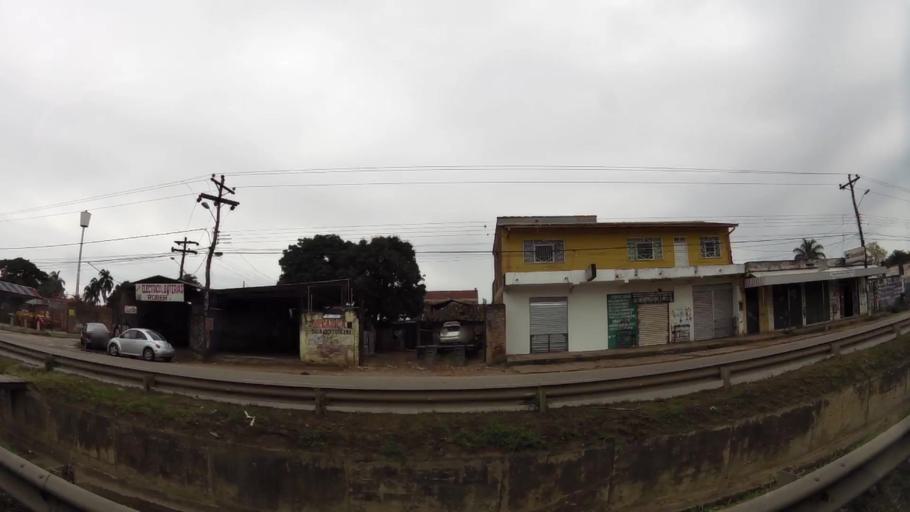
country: BO
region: Santa Cruz
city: Santa Cruz de la Sierra
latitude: -17.8246
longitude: -63.1659
